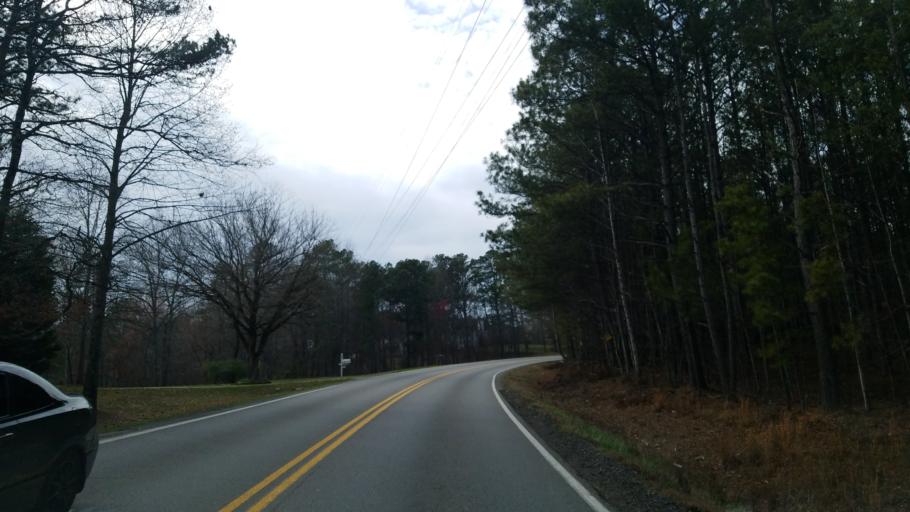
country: US
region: Georgia
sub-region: Cherokee County
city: Ball Ground
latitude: 34.3240
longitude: -84.3544
